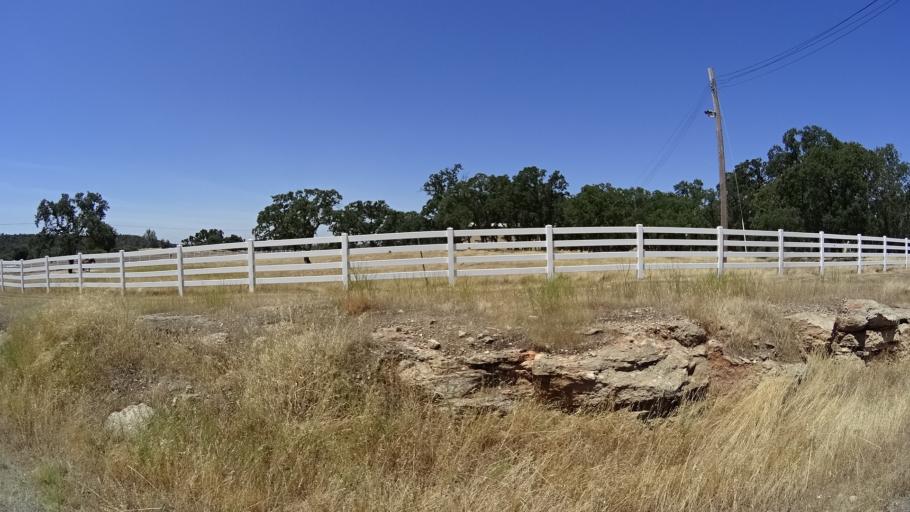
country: US
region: California
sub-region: Calaveras County
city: Valley Springs
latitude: 38.2027
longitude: -120.9052
